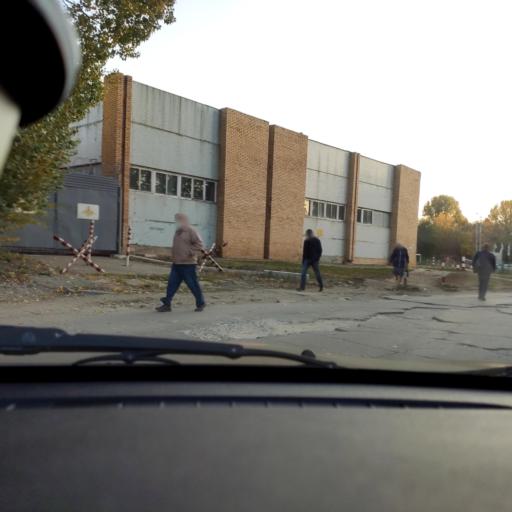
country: RU
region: Samara
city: Tol'yatti
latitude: 53.5370
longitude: 49.3049
